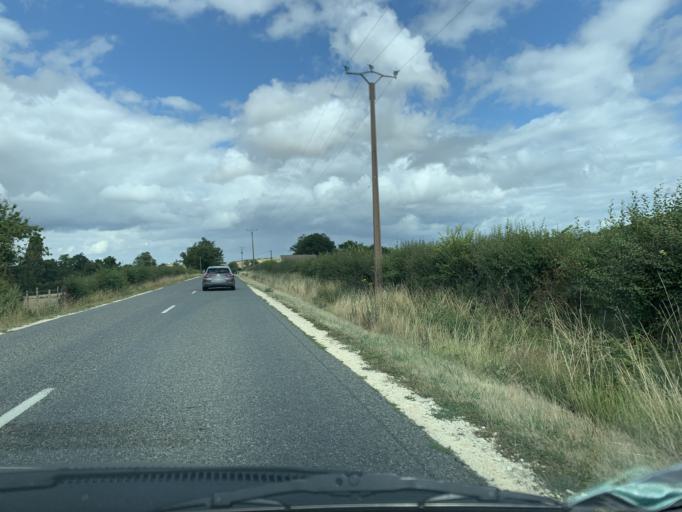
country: FR
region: Bourgogne
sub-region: Departement de la Nievre
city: Varzy
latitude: 47.3981
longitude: 3.4469
